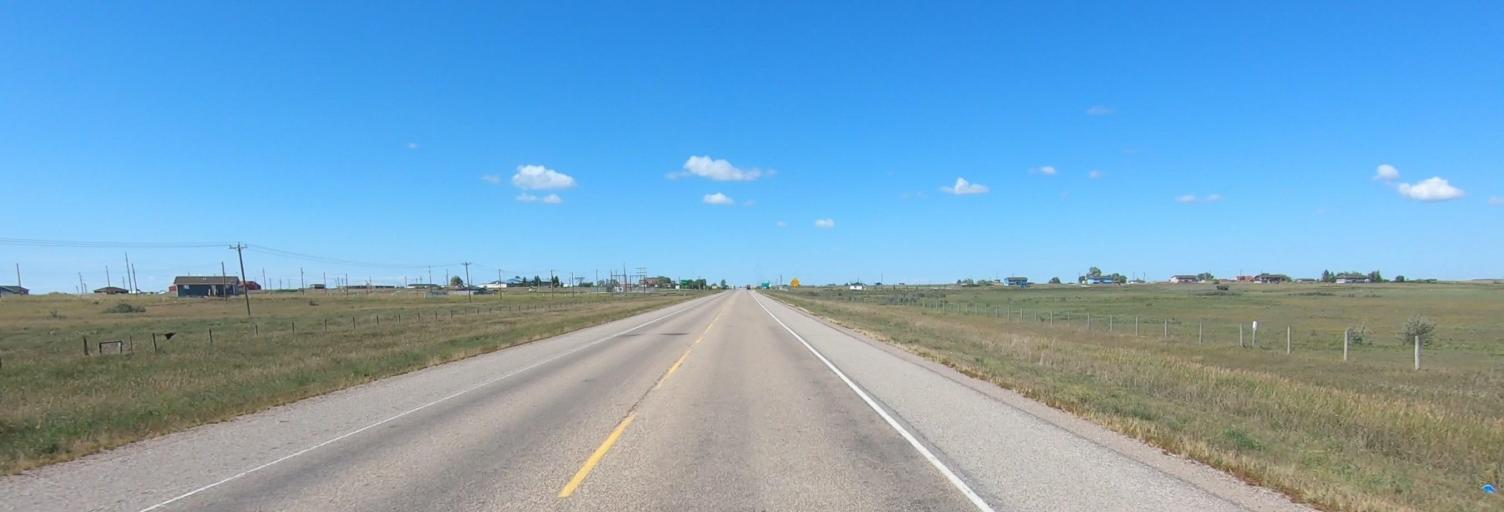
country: CA
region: Alberta
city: Strathmore
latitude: 50.8493
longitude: -113.0430
